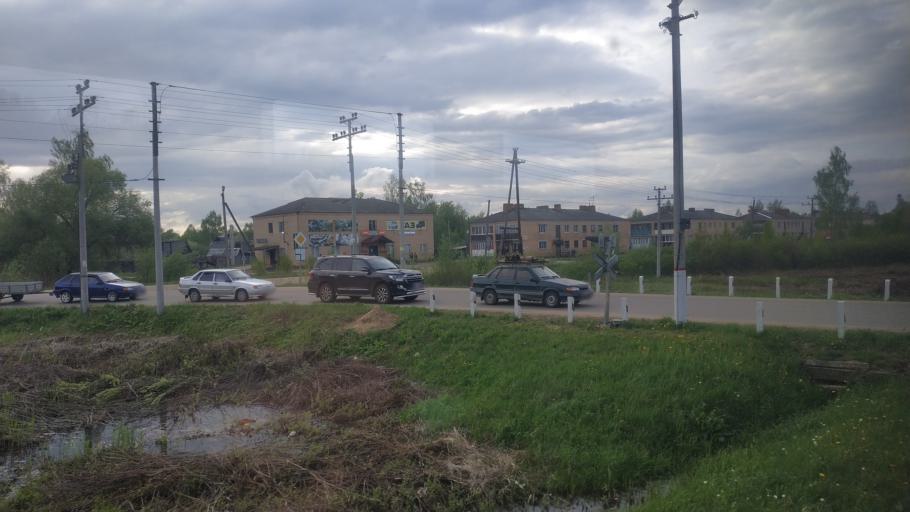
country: RU
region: Smolensk
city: Ugra
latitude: 54.7833
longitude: 34.3420
